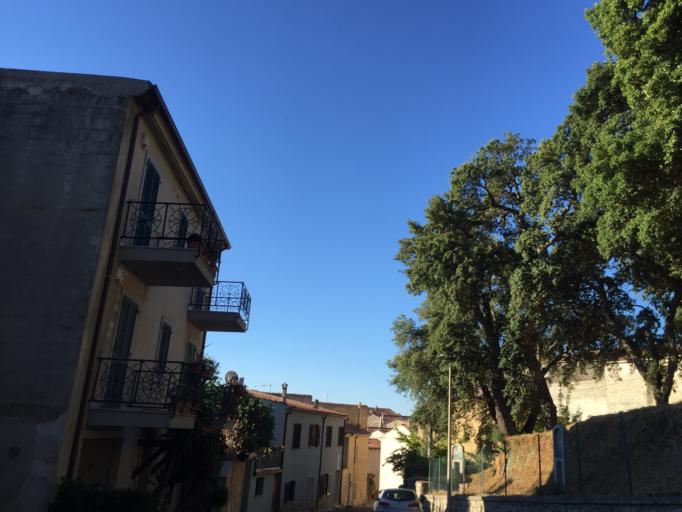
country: IT
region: Sardinia
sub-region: Provincia di Olbia-Tempio
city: Aggius
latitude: 40.9313
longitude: 9.0633
